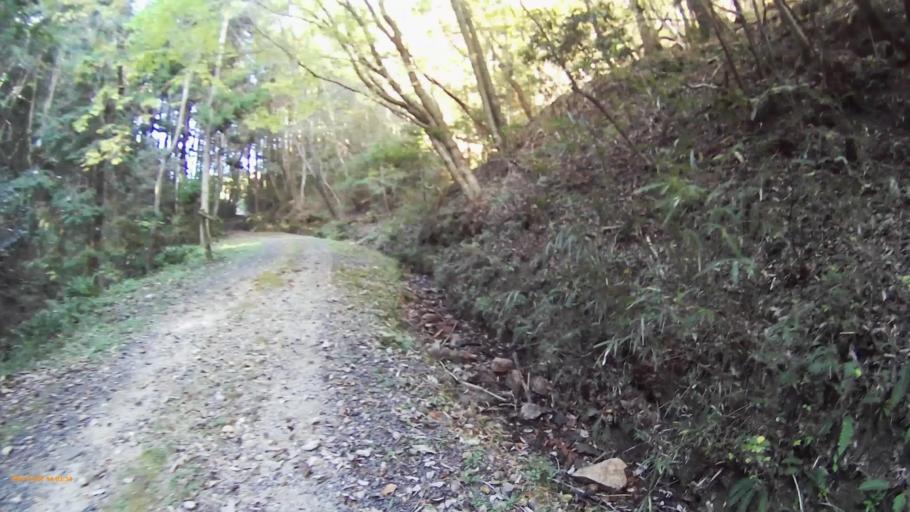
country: JP
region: Gifu
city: Mitake
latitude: 35.4261
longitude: 137.1857
